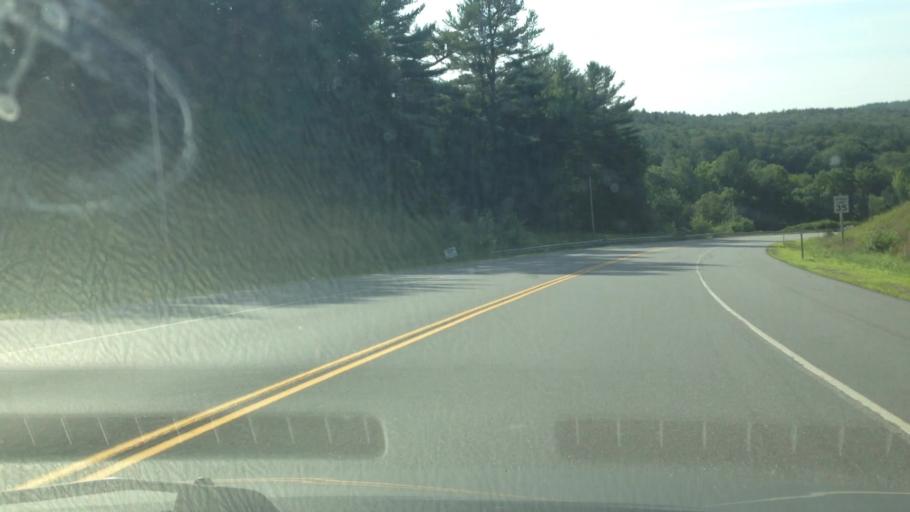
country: US
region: New Hampshire
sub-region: Cheshire County
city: Keene
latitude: 42.9545
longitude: -72.2713
